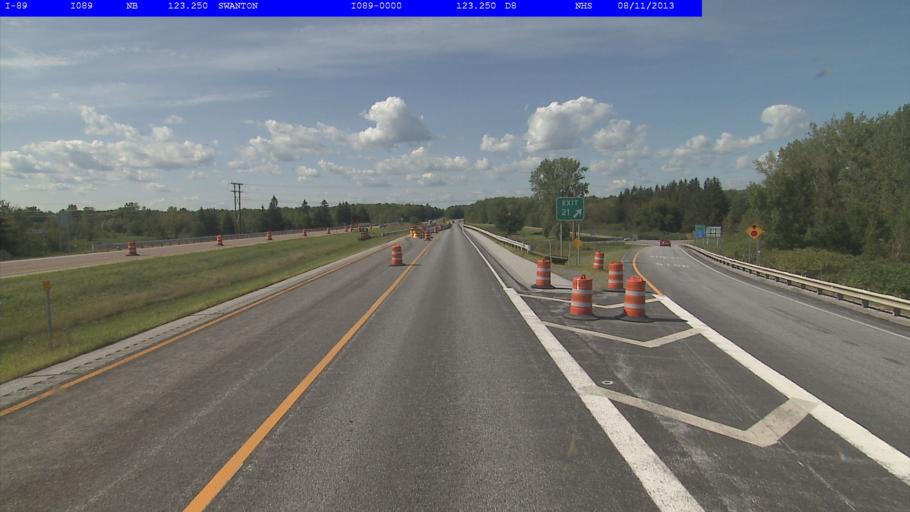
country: US
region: Vermont
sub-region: Franklin County
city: Swanton
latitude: 44.9207
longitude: -73.1066
